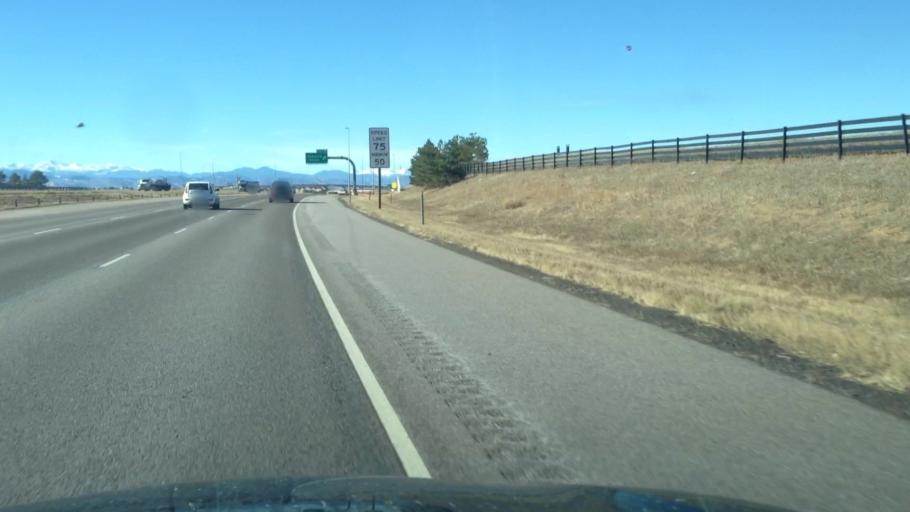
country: US
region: Colorado
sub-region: Douglas County
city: Meridian
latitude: 39.5514
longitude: -104.8537
